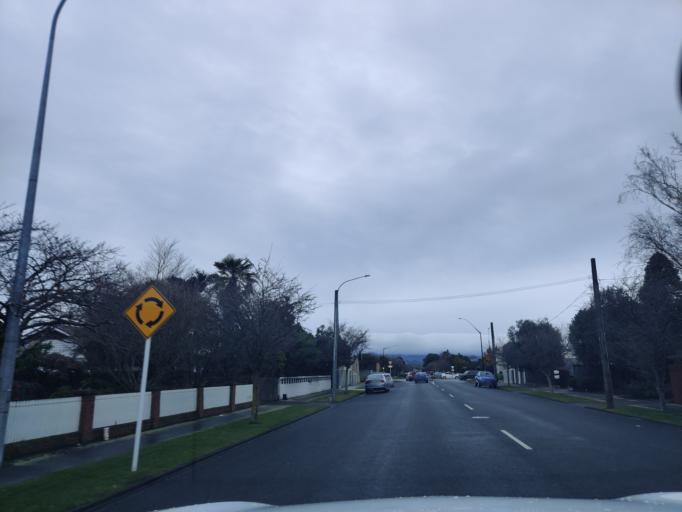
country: NZ
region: Manawatu-Wanganui
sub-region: Palmerston North City
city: Palmerston North
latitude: -40.3443
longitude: 175.6160
